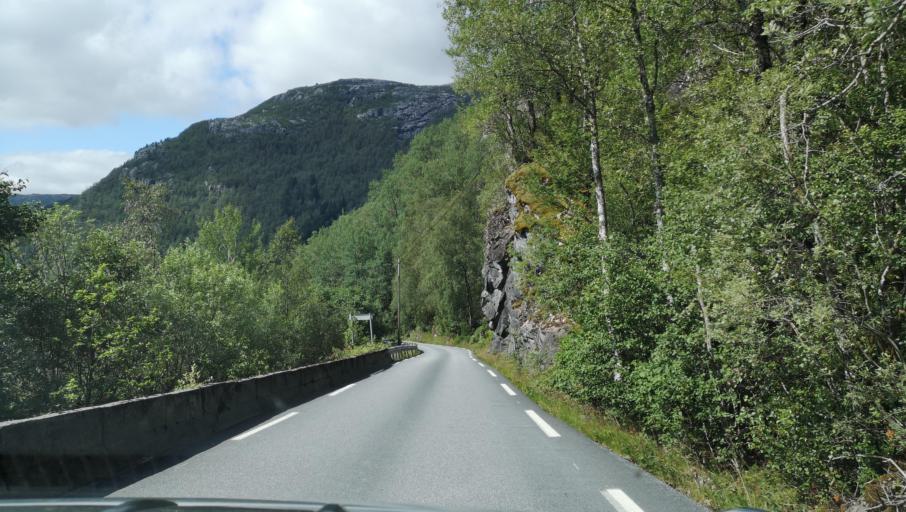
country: NO
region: Hordaland
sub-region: Modalen
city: Mo
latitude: 60.7818
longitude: 5.9464
